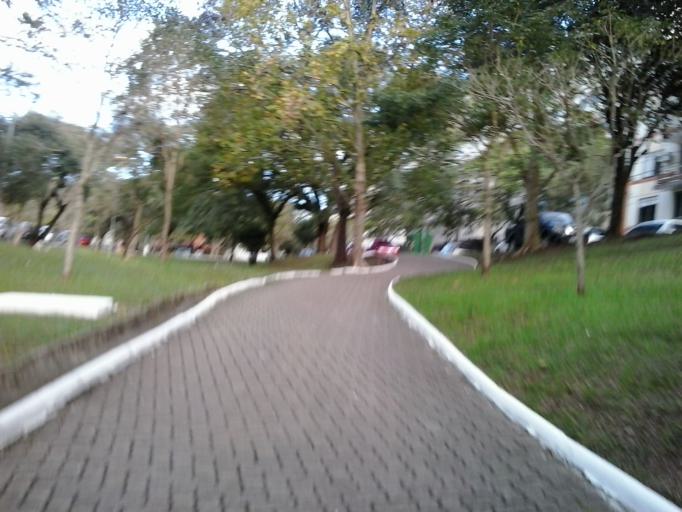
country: BR
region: Rio Grande do Sul
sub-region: Santa Maria
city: Santa Maria
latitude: -29.6881
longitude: -53.8020
